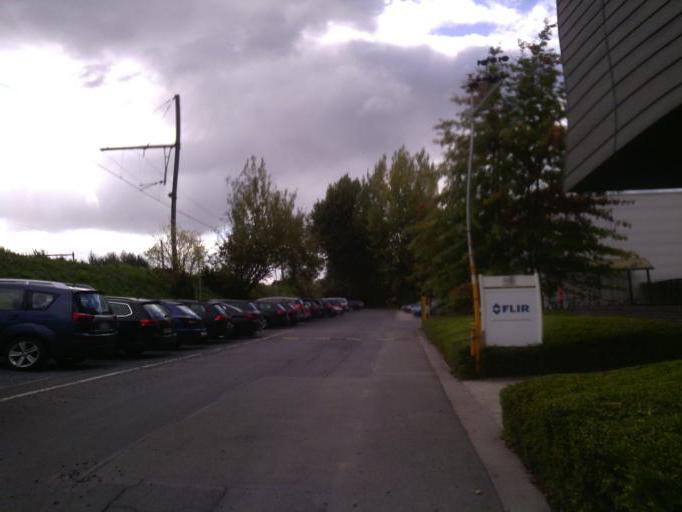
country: BE
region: Flanders
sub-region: Provincie West-Vlaanderen
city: Kortrijk
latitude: 50.8115
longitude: 3.2319
